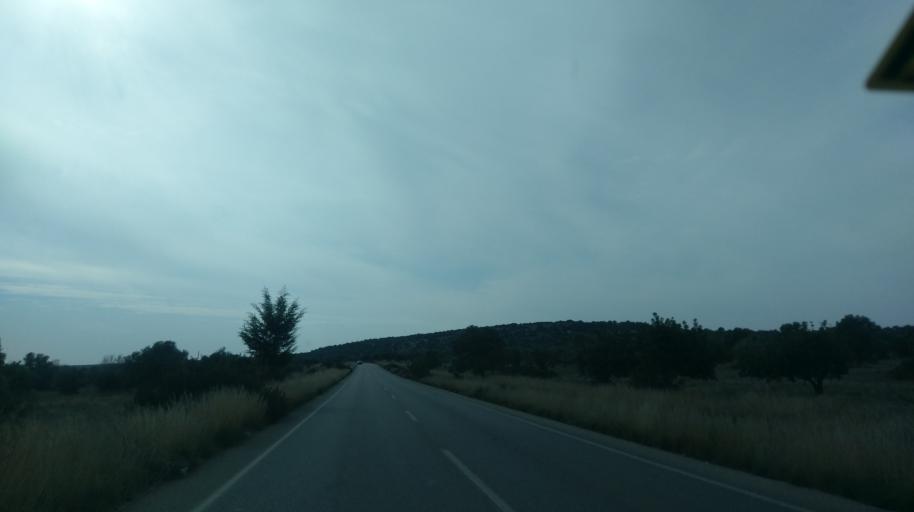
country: CY
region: Ammochostos
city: Leonarisso
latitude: 35.4106
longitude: 34.1129
